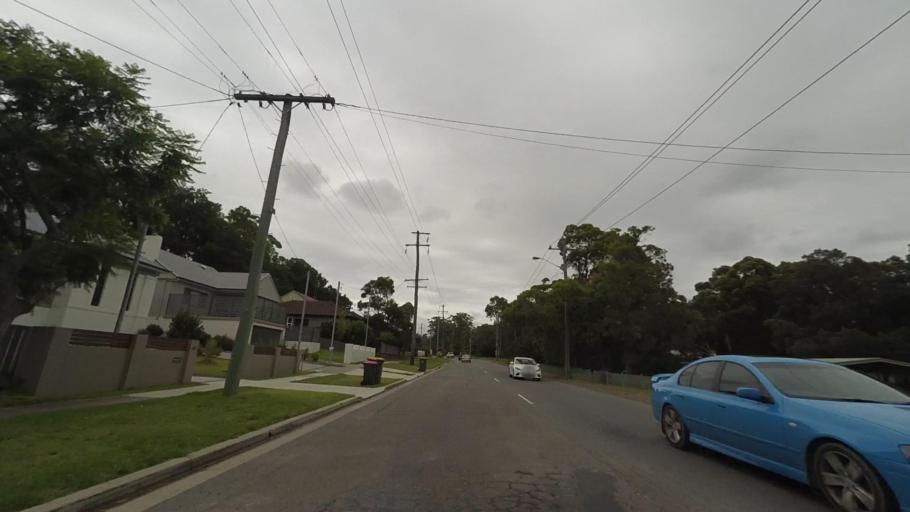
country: AU
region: New South Wales
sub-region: Lake Macquarie Shire
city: Kotara
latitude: -32.9427
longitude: 151.6980
